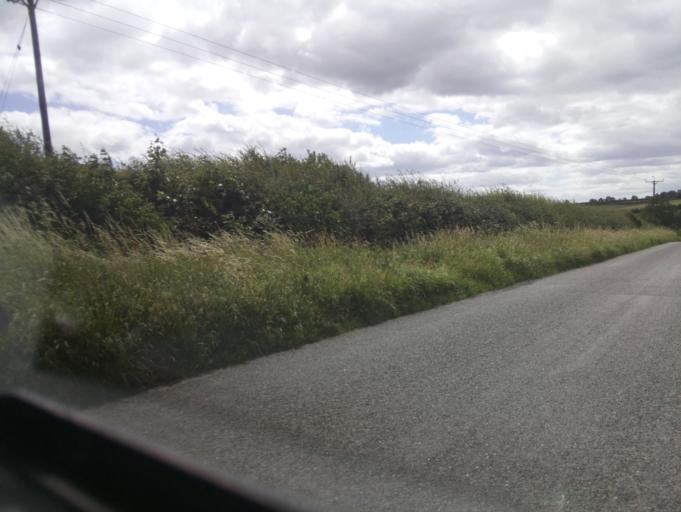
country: GB
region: England
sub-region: Nottinghamshire
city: Ruddington
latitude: 52.8609
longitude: -1.0966
